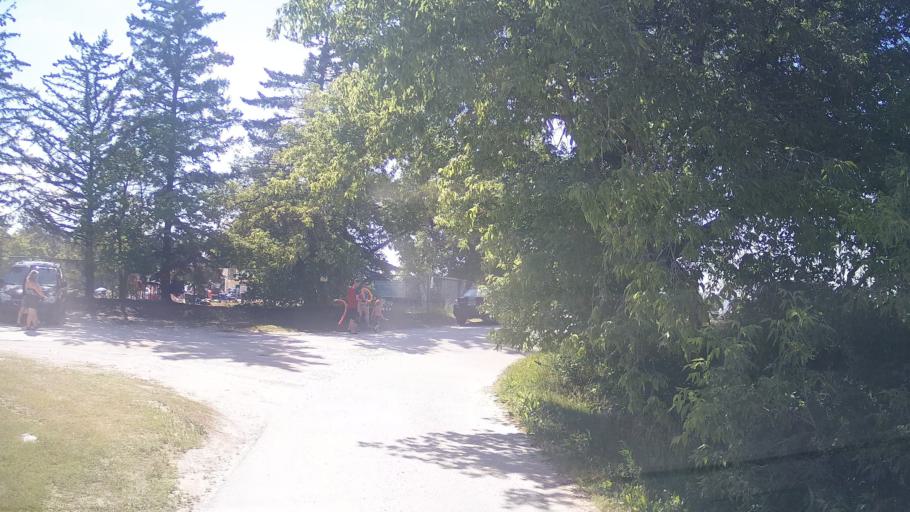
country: CA
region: Manitoba
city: Stonewall
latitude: 50.1418
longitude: -97.3274
